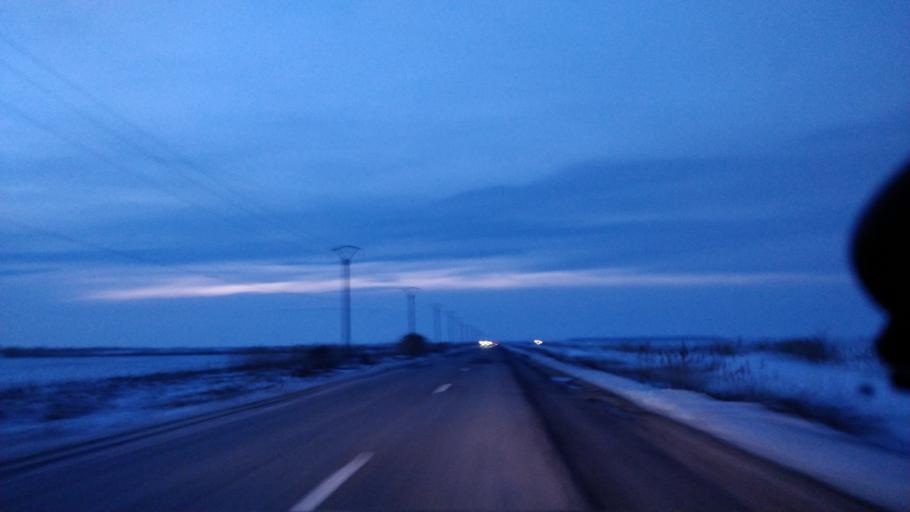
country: RO
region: Galati
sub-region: Comuna Liesti
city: Liesti
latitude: 45.5922
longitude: 27.4791
